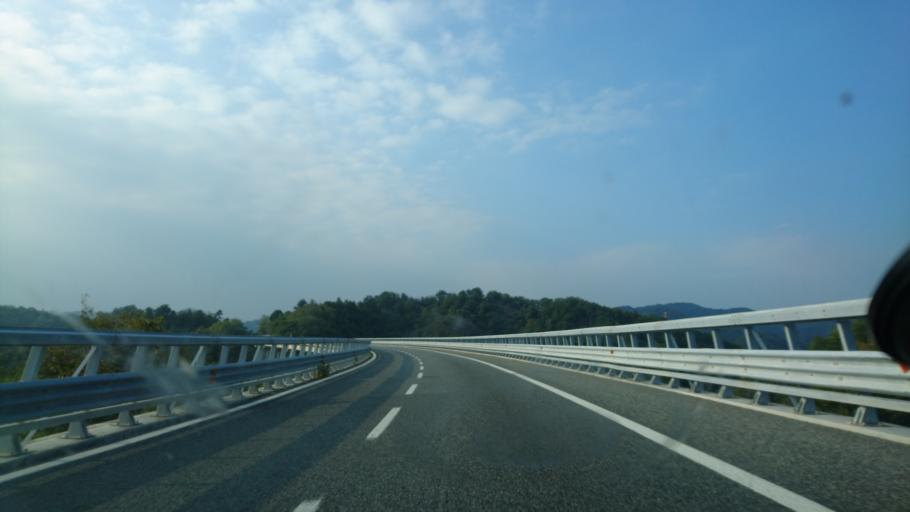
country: IT
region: Liguria
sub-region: Provincia di Savona
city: Altare
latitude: 44.3414
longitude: 8.3788
